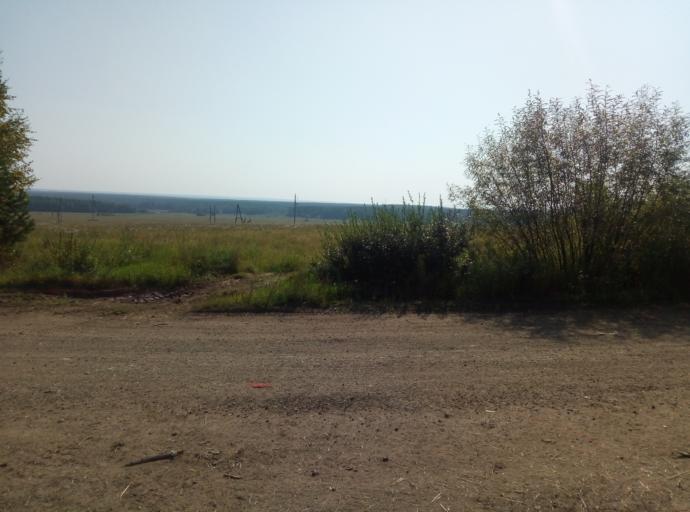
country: RU
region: Sverdlovsk
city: Rudnichnyy
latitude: 59.7225
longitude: 60.2905
